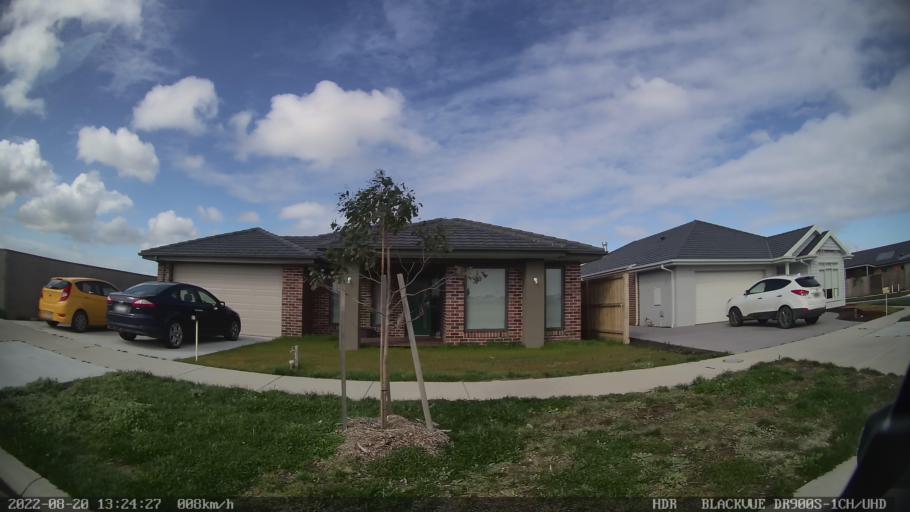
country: AU
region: Victoria
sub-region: Bass Coast
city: North Wonthaggi
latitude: -38.5951
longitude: 145.6112
